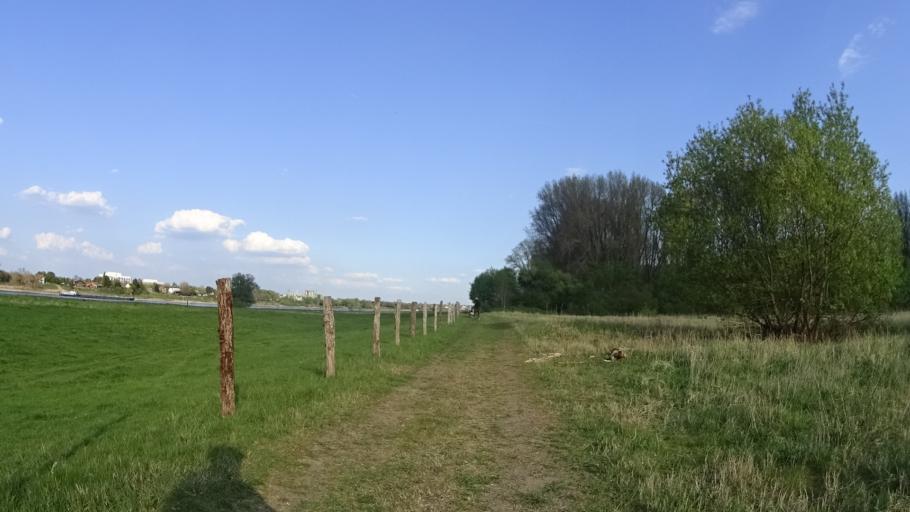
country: DE
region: North Rhine-Westphalia
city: Monheim am Rhein
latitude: 51.0672
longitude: 6.8789
